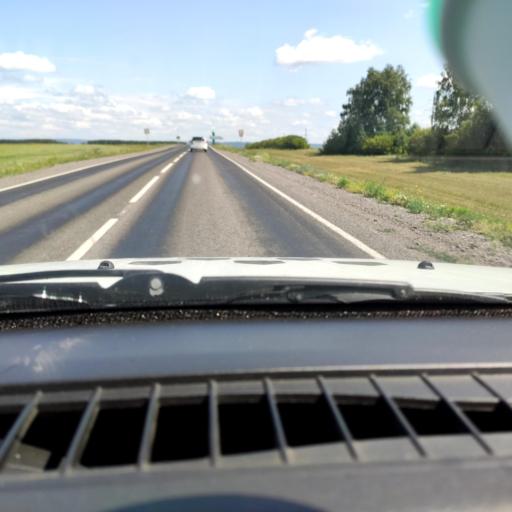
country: RU
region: Bashkortostan
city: Verkhniye Kigi
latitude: 55.4598
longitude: 58.4627
